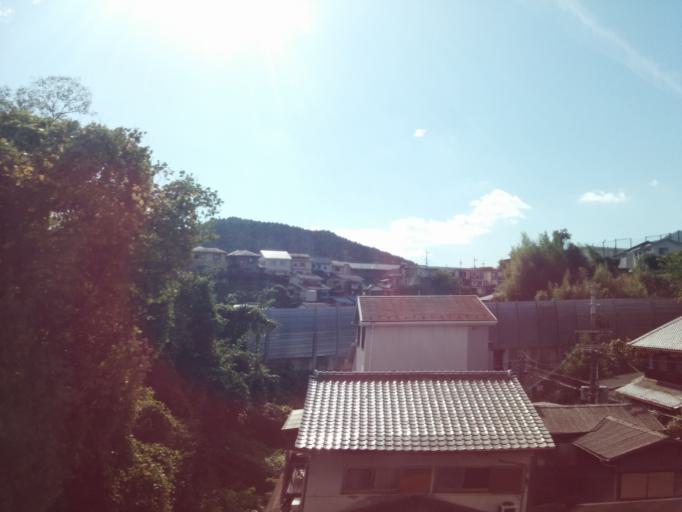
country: JP
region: Shiga Prefecture
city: Otsu-shi
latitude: 34.9704
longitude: 135.9003
